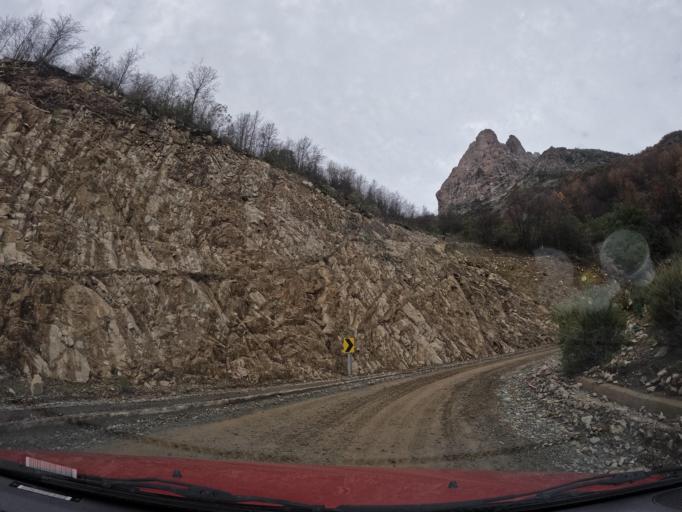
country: CL
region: Maule
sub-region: Provincia de Linares
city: Colbun
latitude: -35.8550
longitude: -71.1873
